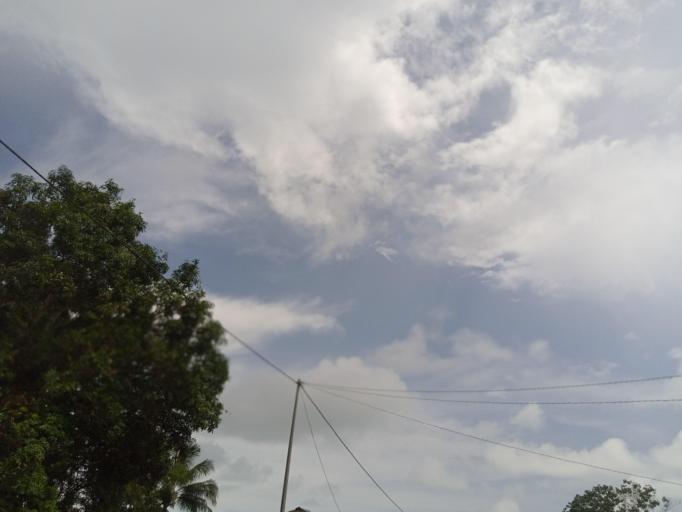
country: SL
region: Northern Province
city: Sawkta
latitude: 8.6277
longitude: -13.2064
